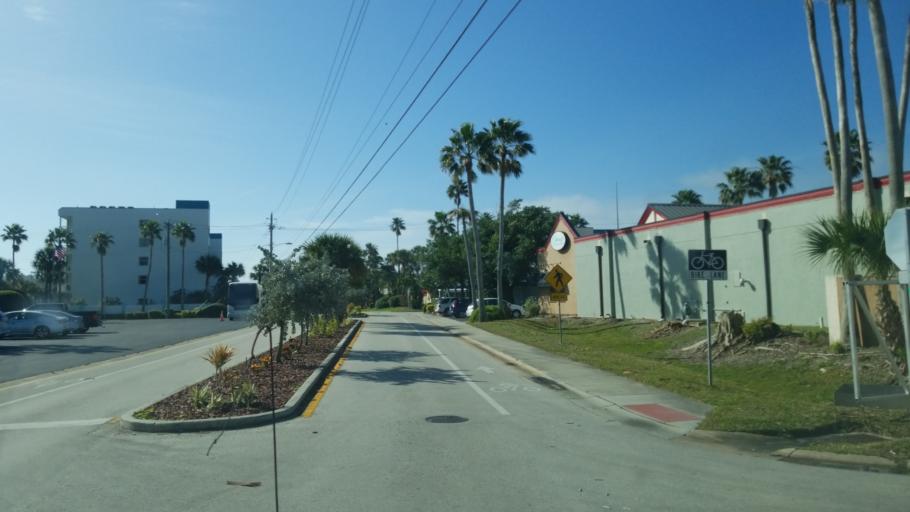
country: US
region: Florida
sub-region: Brevard County
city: Cape Canaveral
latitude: 28.3696
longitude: -80.6041
